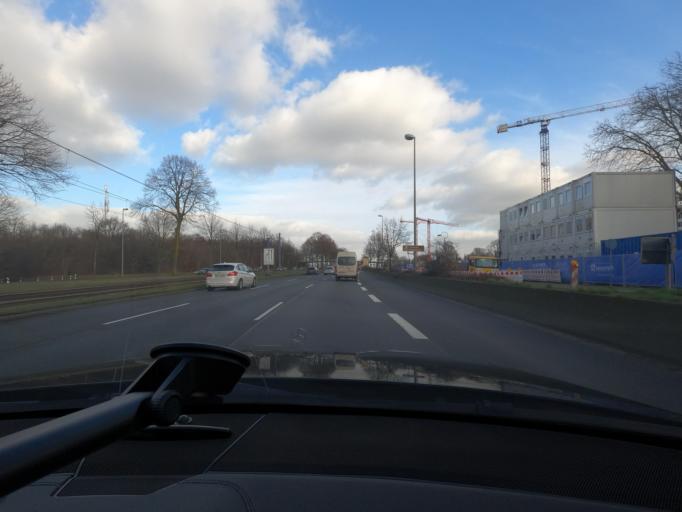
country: DE
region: North Rhine-Westphalia
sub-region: Regierungsbezirk Arnsberg
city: Dortmund
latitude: 51.5028
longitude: 7.5202
